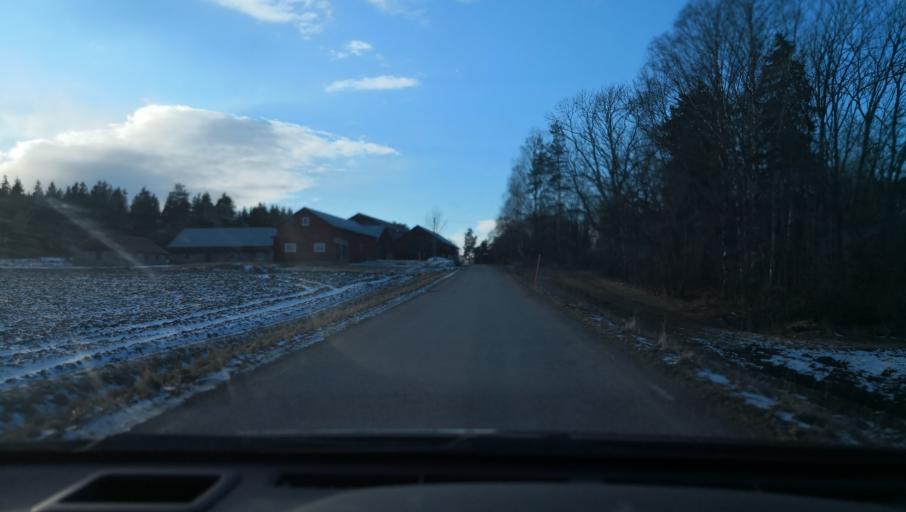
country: SE
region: Uppsala
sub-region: Enkopings Kommun
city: Irsta
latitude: 59.6581
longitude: 16.7929
